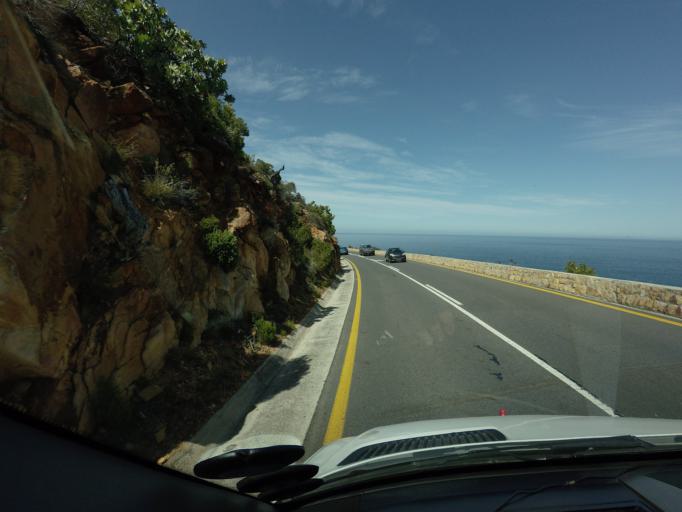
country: ZA
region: Western Cape
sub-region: Overberg District Municipality
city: Grabouw
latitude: -34.2154
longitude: 18.8346
